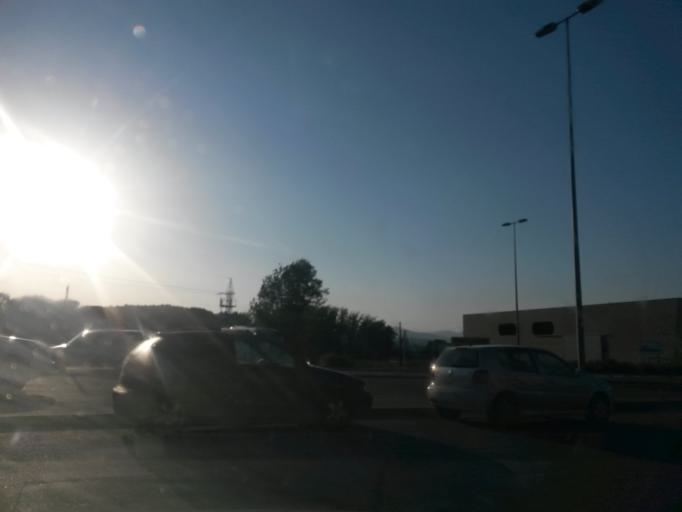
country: ES
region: Catalonia
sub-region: Provincia de Girona
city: Fornells de la Selva
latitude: 41.9316
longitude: 2.7955
